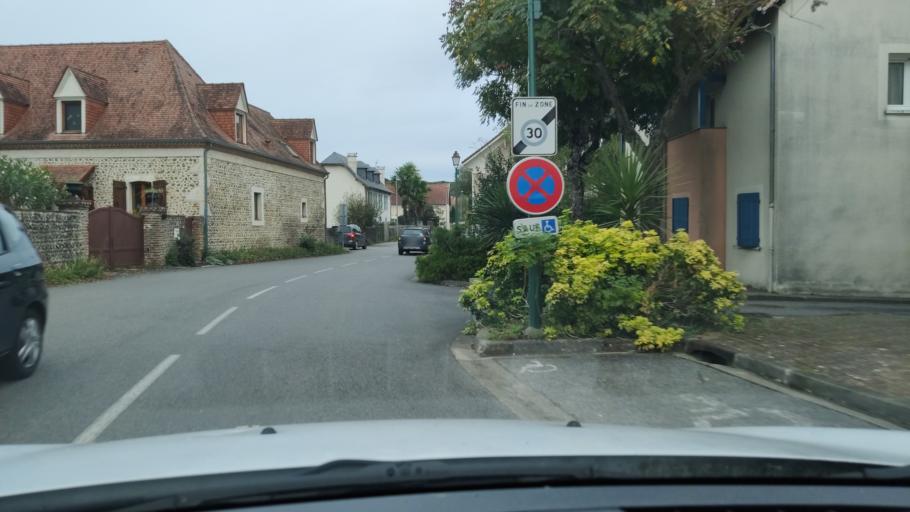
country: FR
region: Aquitaine
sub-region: Departement des Pyrenees-Atlantiques
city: Sauvagnon
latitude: 43.4046
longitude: -0.3869
